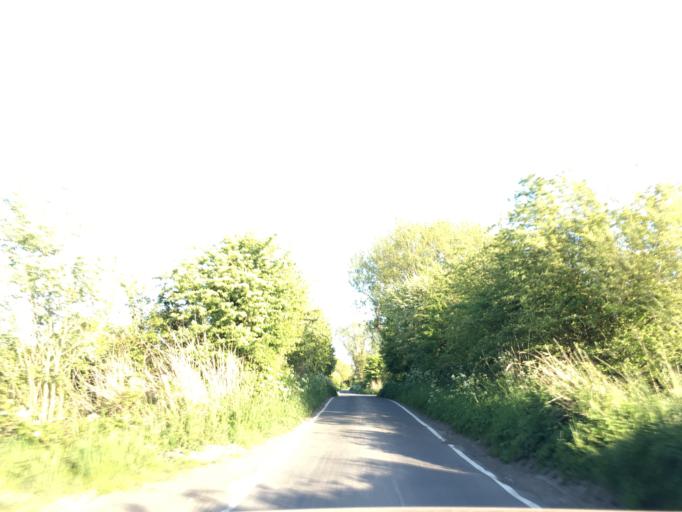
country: GB
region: Wales
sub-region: Newport
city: Marshfield
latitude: 51.5157
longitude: -3.0651
